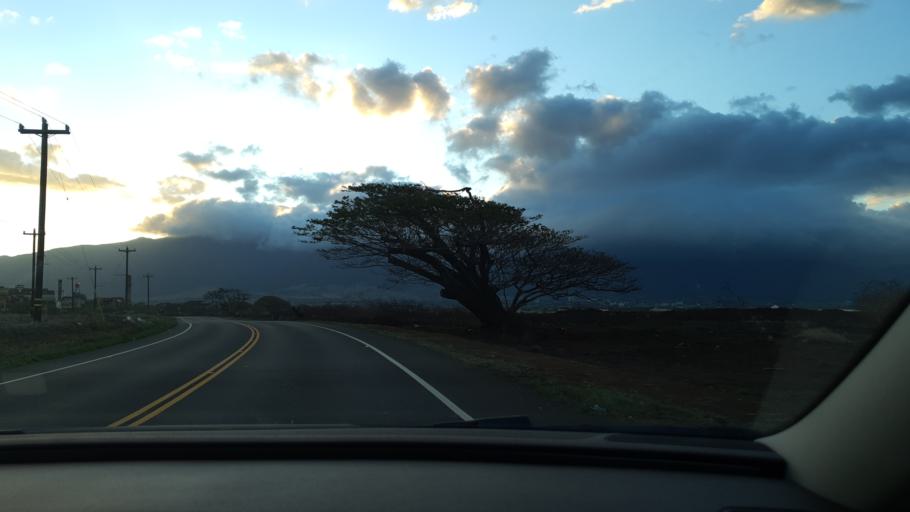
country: US
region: Hawaii
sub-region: Maui County
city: Kahului
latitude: 20.8711
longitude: -156.4455
